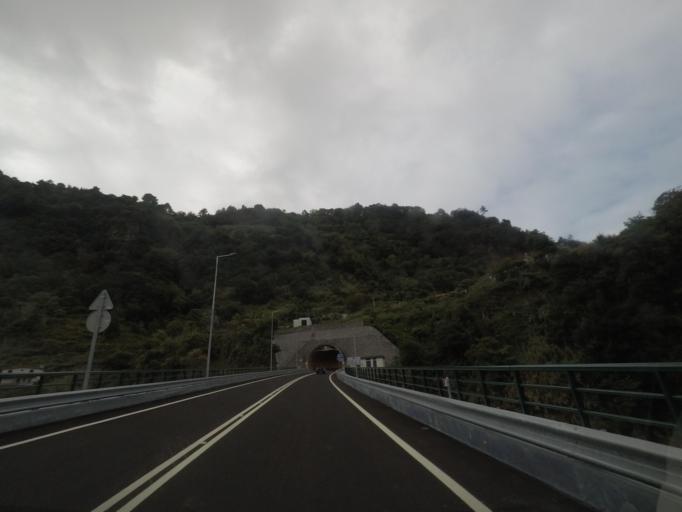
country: PT
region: Madeira
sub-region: Santana
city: Santana
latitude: 32.8166
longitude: -16.9023
